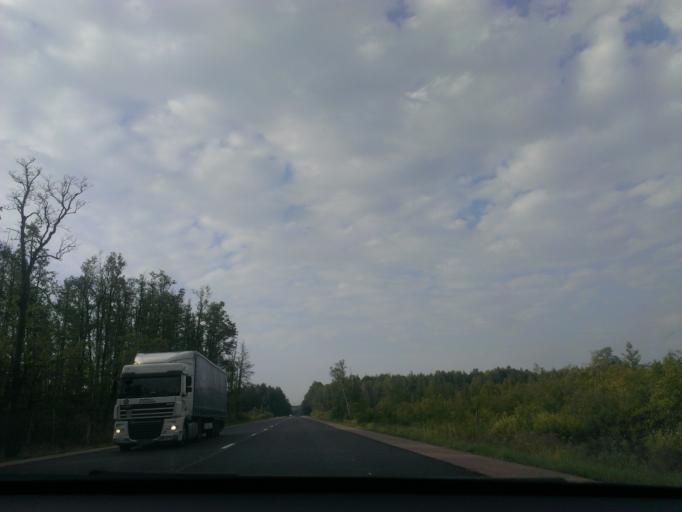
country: LV
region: Lecava
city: Iecava
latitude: 56.7022
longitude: 24.2444
